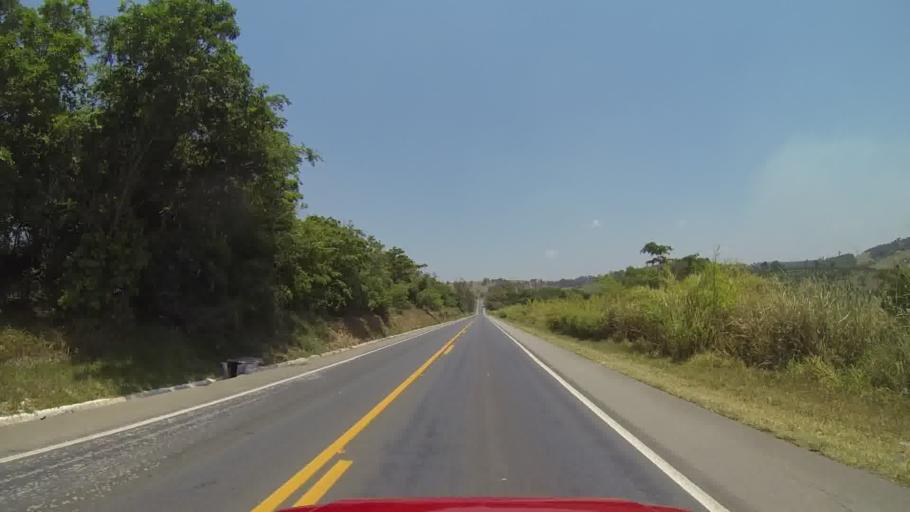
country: BR
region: Minas Gerais
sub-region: Itapecerica
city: Itapecerica
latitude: -20.3317
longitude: -45.2298
